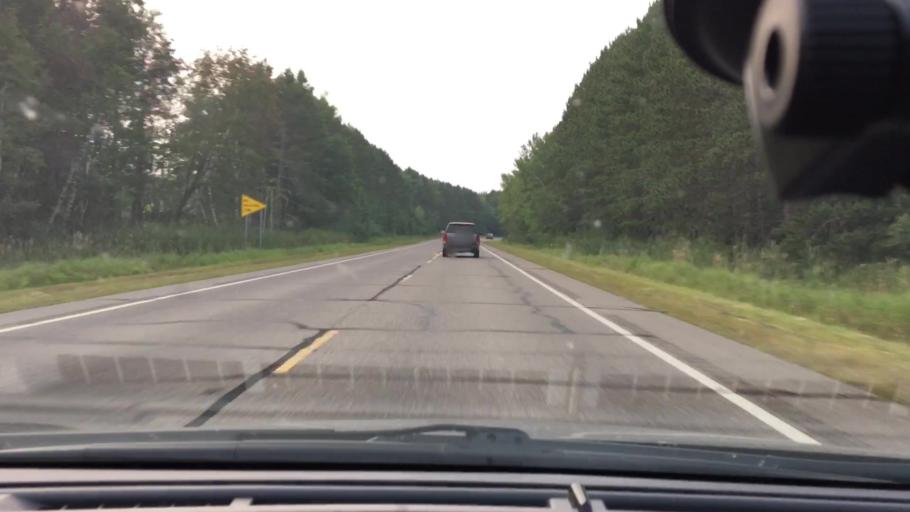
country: US
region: Minnesota
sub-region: Crow Wing County
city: Crosby
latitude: 46.4429
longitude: -93.8779
